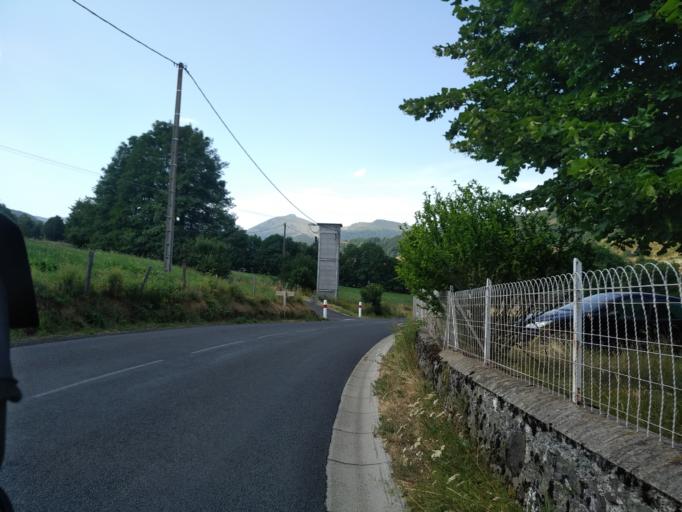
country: FR
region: Auvergne
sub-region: Departement du Cantal
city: Riom-es-Montagnes
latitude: 45.1674
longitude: 2.7139
